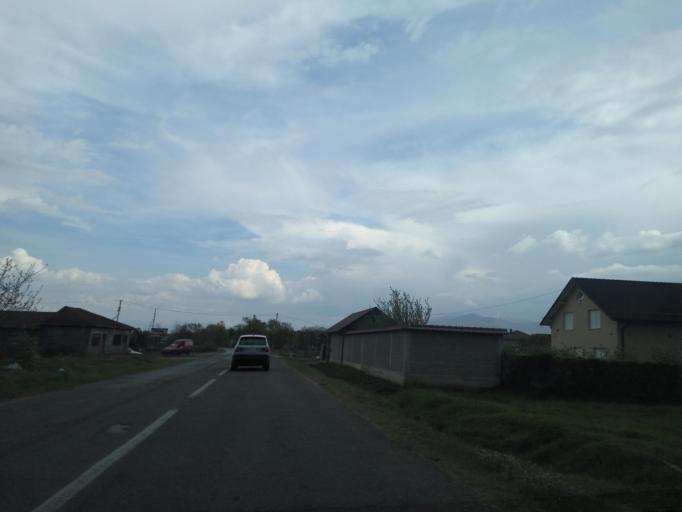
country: XK
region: Gjakova
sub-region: Komuna e Gjakoves
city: Gjakove
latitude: 42.3731
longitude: 20.3471
